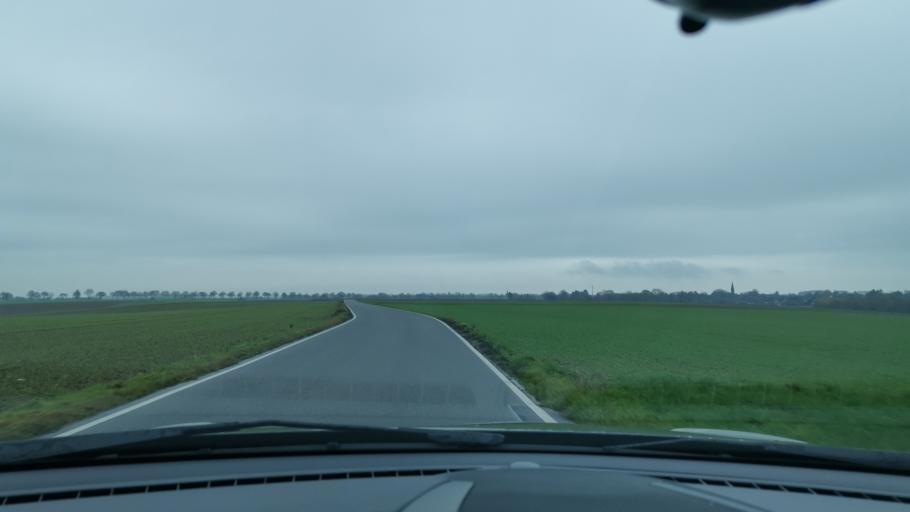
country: DE
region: North Rhine-Westphalia
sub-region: Regierungsbezirk Dusseldorf
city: Juchen
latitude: 51.1164
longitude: 6.5242
